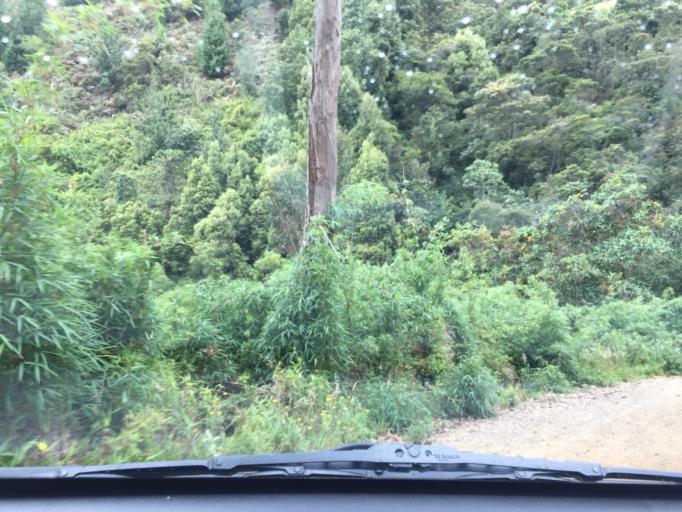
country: CO
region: Cundinamarca
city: Tabio
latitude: 4.9129
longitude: -74.1244
